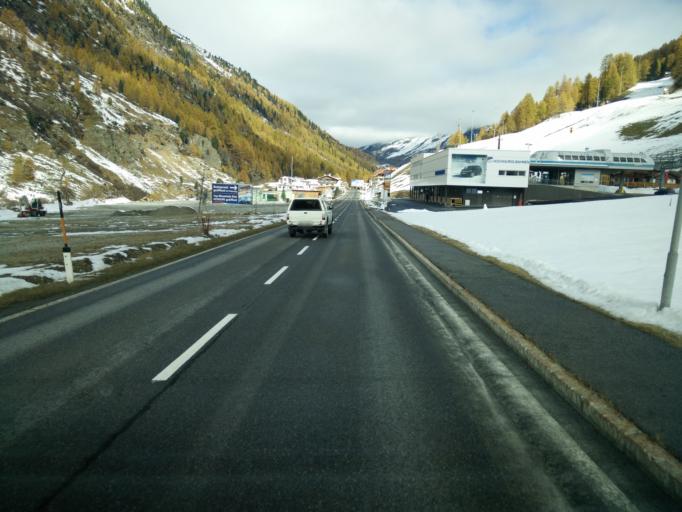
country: AT
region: Tyrol
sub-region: Politischer Bezirk Imst
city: Soelden
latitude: 46.8967
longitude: 11.0404
